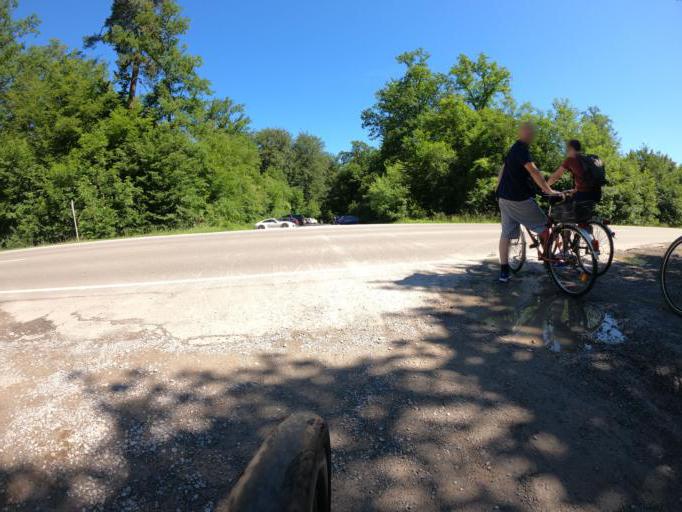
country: DE
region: Baden-Wuerttemberg
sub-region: Regierungsbezirk Stuttgart
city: Gerlingen
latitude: 48.7557
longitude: 9.1015
